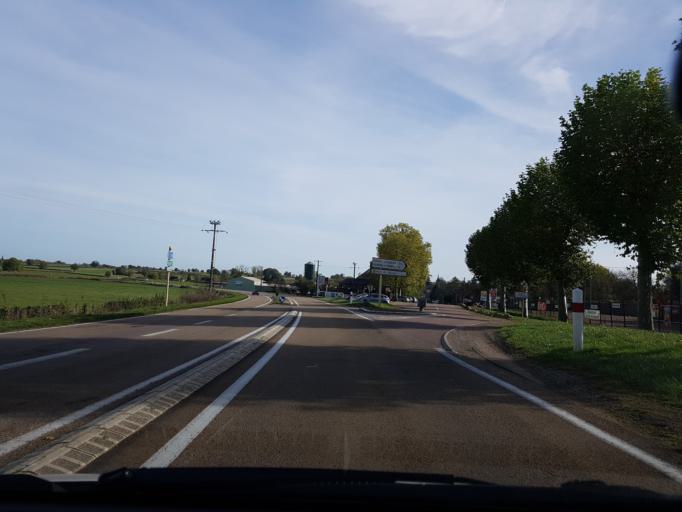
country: FR
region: Bourgogne
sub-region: Departement de l'Yonne
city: Avallon
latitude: 47.4748
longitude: 4.0175
